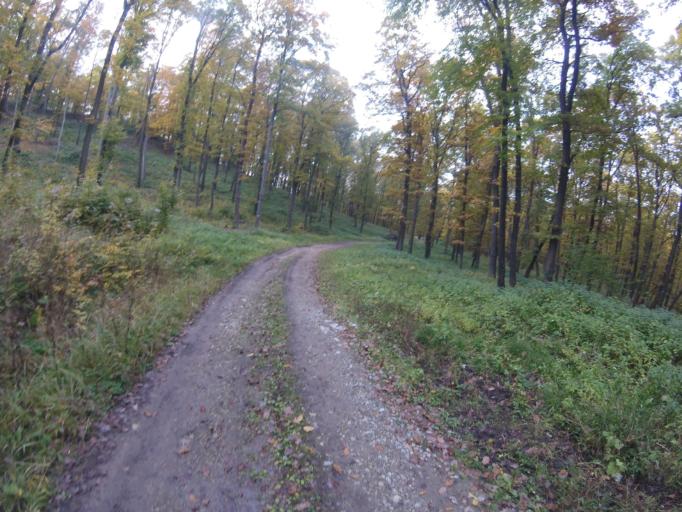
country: HU
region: Borsod-Abauj-Zemplen
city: Putnok
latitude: 48.2370
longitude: 20.4317
